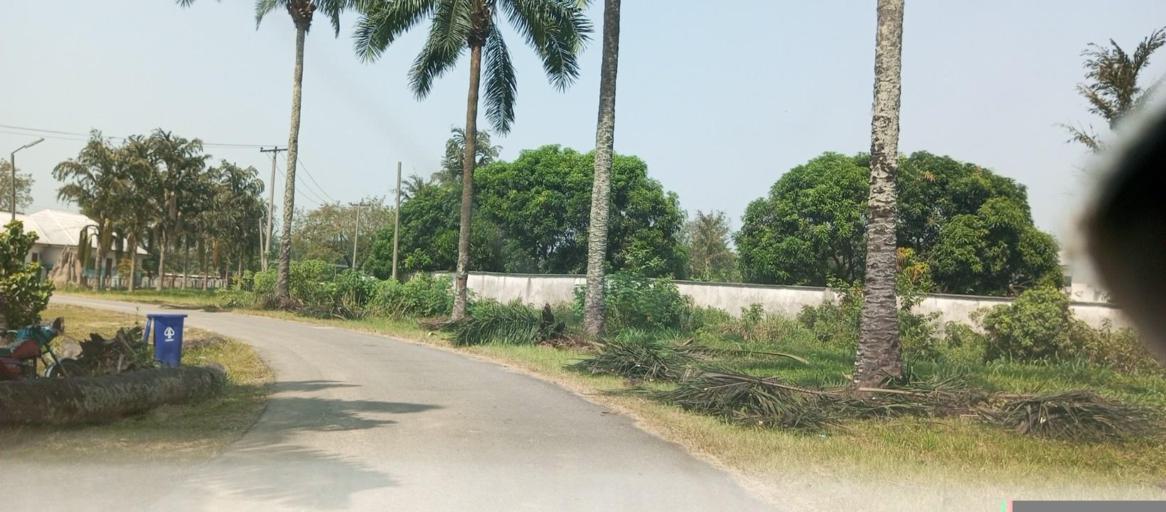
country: NG
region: Rivers
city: Emuoha
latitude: 4.9009
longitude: 6.9085
